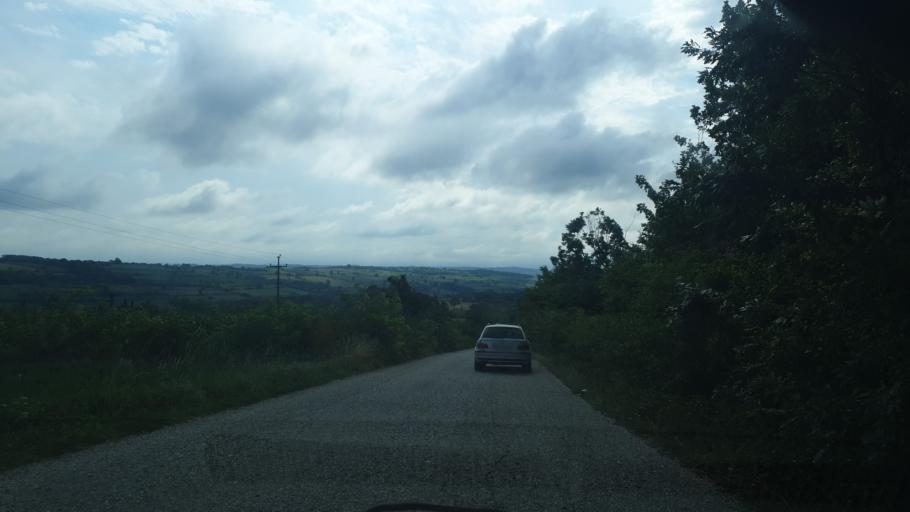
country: RS
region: Central Serbia
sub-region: Sumadijski Okrug
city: Kragujevac
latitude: 44.0971
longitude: 20.7841
